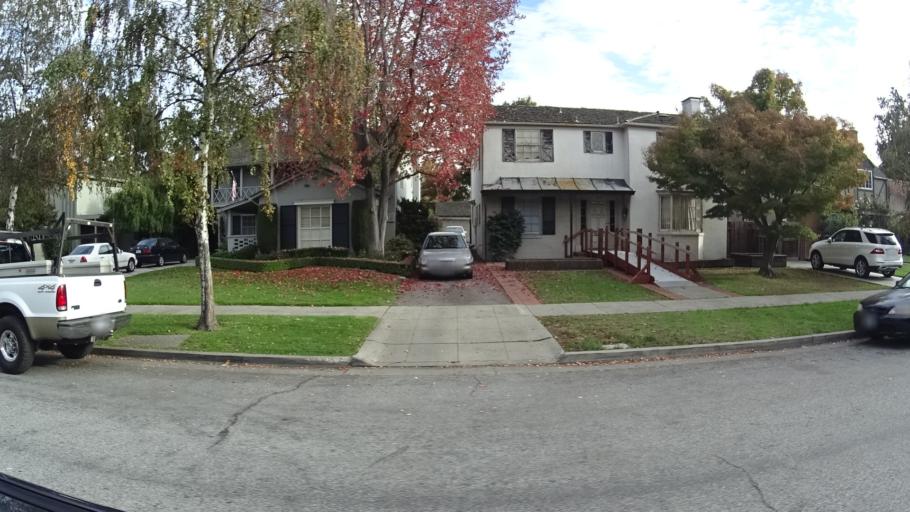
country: US
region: California
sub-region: Santa Clara County
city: Buena Vista
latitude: 37.3295
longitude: -121.9213
